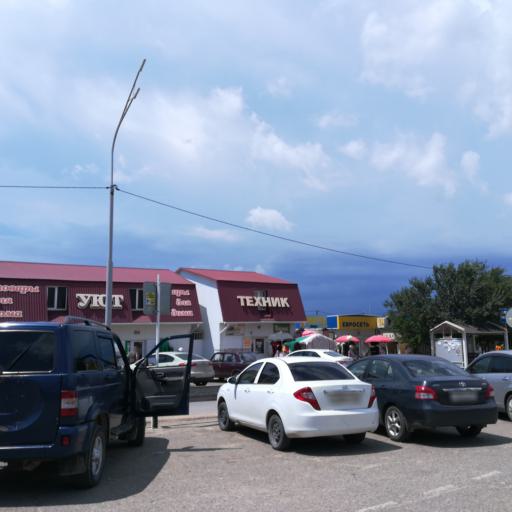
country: RU
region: Krasnodarskiy
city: Taman'
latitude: 45.2143
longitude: 36.7196
